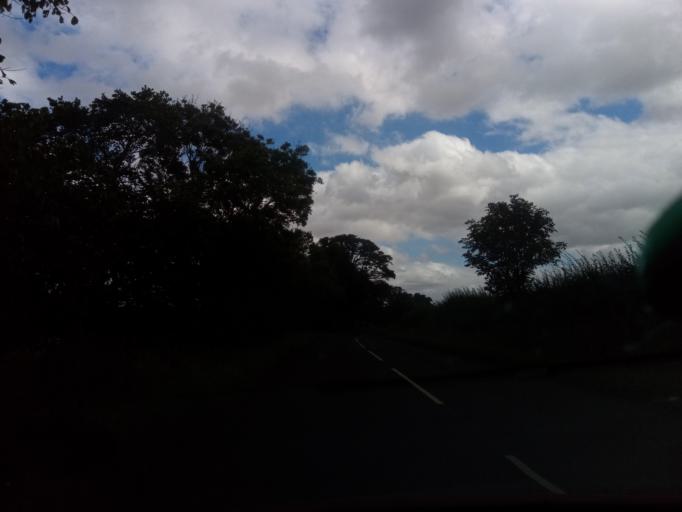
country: GB
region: Scotland
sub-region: The Scottish Borders
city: Kelso
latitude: 55.6016
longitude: -2.4156
